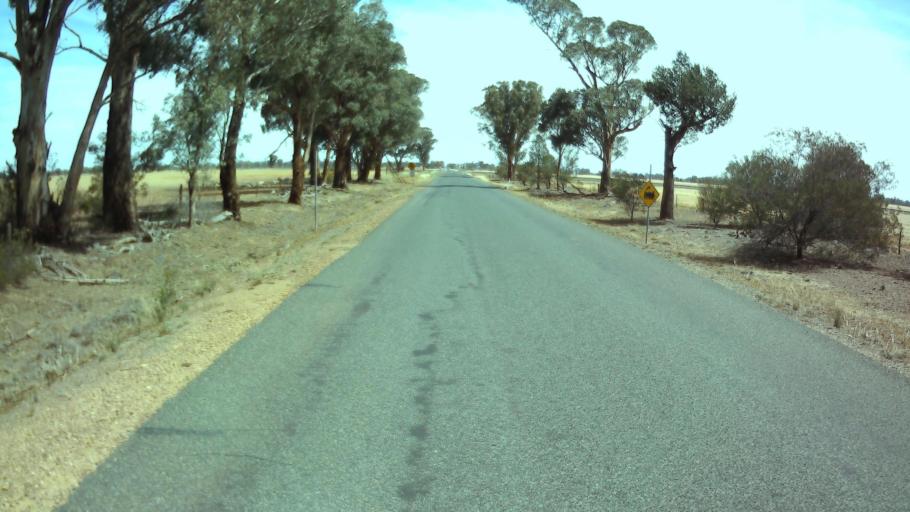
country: AU
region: New South Wales
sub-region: Weddin
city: Grenfell
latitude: -33.9813
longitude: 147.7779
